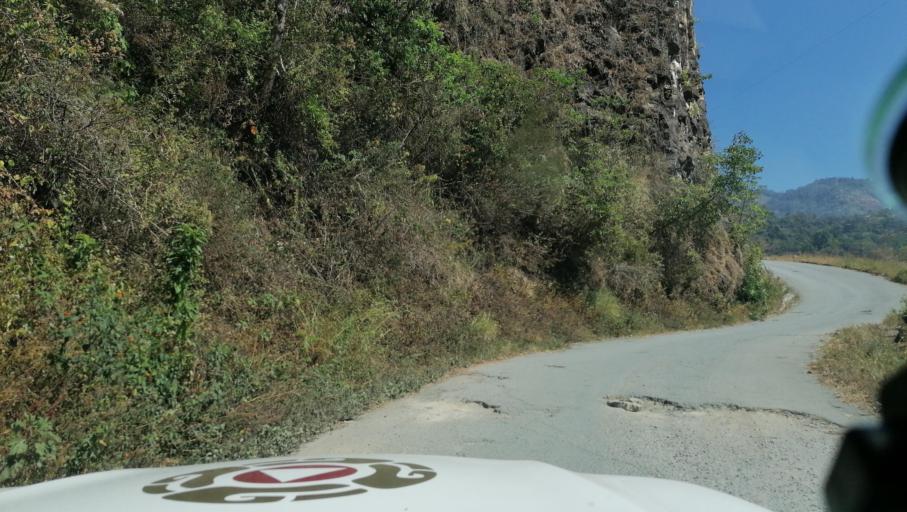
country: GT
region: San Marcos
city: Tacana
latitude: 15.1891
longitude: -92.1863
